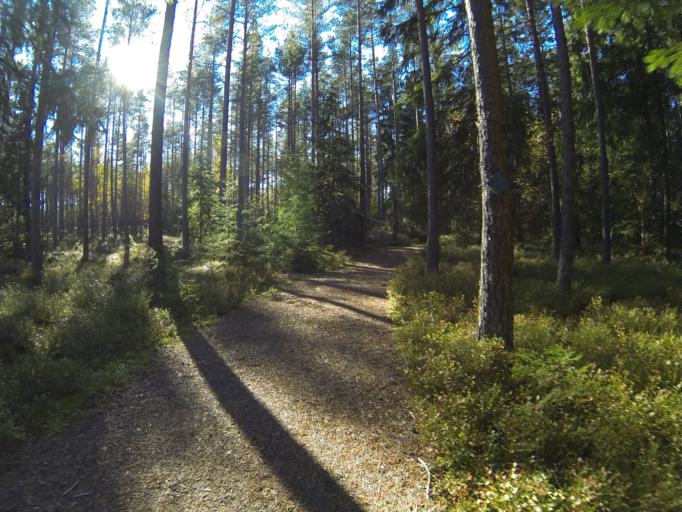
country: FI
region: Varsinais-Suomi
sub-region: Salo
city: Saerkisalo
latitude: 60.1987
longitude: 22.9321
